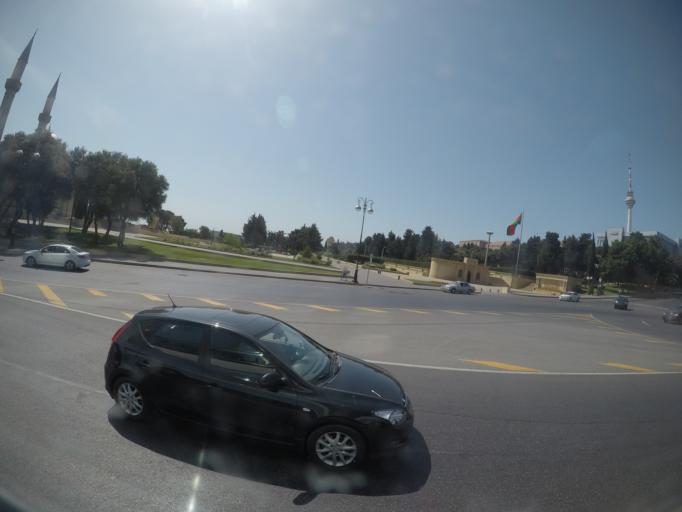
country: AZ
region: Baki
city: Badamdar
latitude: 40.3587
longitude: 49.8271
